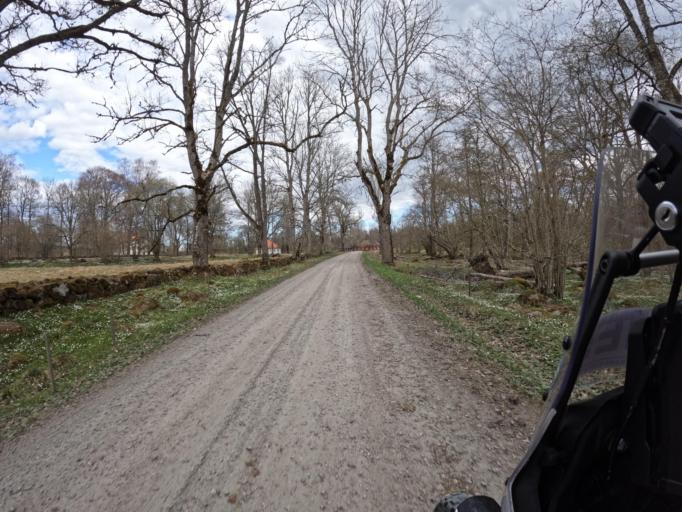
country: SE
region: Joenkoeping
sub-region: Mullsjo Kommun
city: Mullsjoe
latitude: 57.8856
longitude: 13.6444
